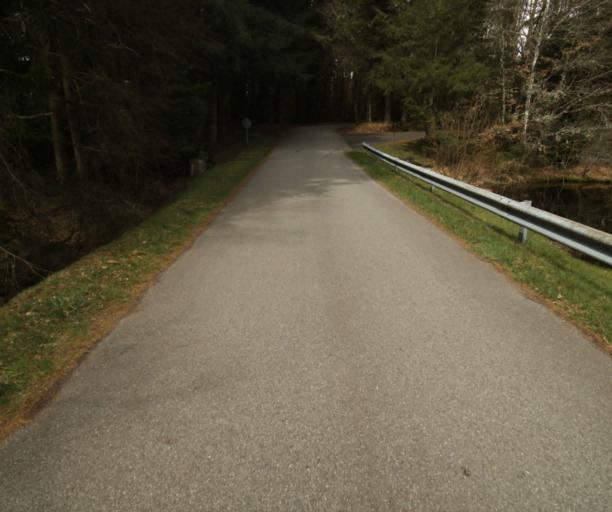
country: FR
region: Limousin
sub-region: Departement de la Correze
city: Correze
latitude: 45.3394
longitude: 1.9496
